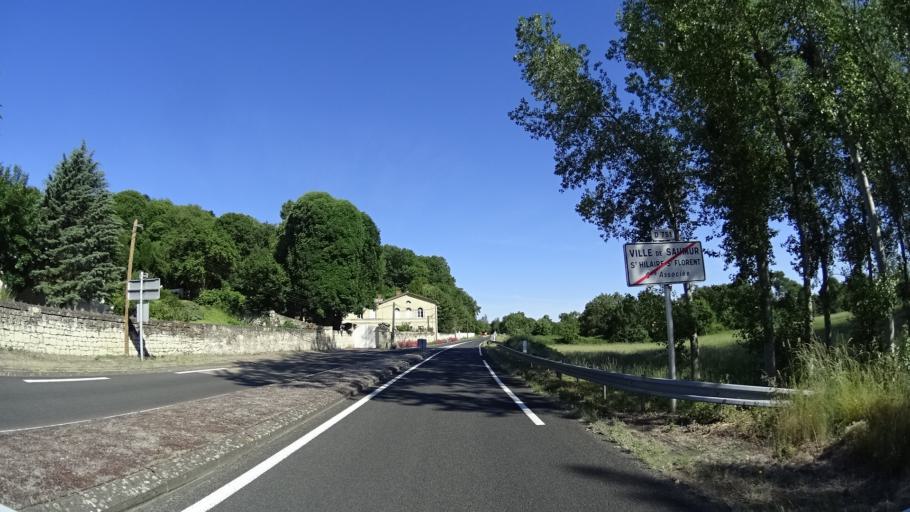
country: FR
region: Pays de la Loire
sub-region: Departement de Maine-et-Loire
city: Saumur
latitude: 47.2803
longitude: -0.1203
